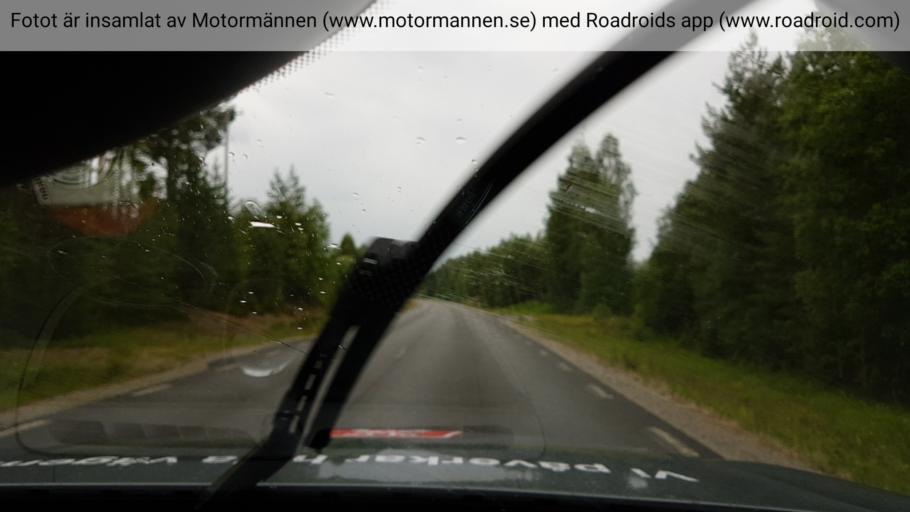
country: SE
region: Jaemtland
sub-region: Braecke Kommun
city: Braecke
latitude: 62.4104
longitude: 15.0158
